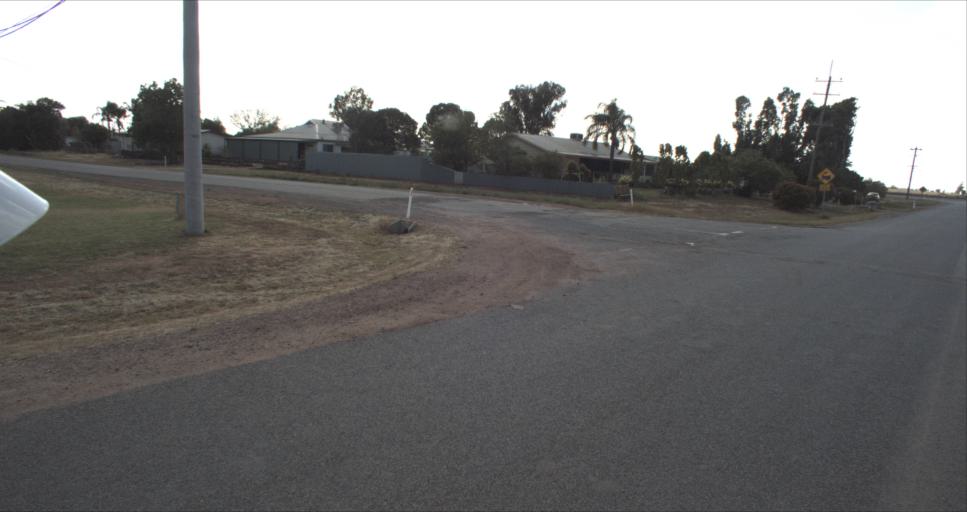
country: AU
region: New South Wales
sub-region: Murrumbidgee Shire
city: Darlington Point
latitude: -34.5160
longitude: 146.1836
